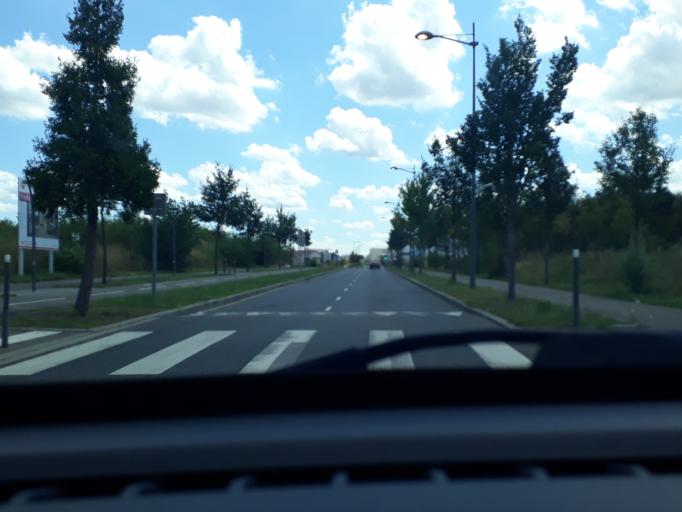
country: FR
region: Rhone-Alpes
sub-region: Departement du Rhone
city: Bron
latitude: 45.7090
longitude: 4.9164
